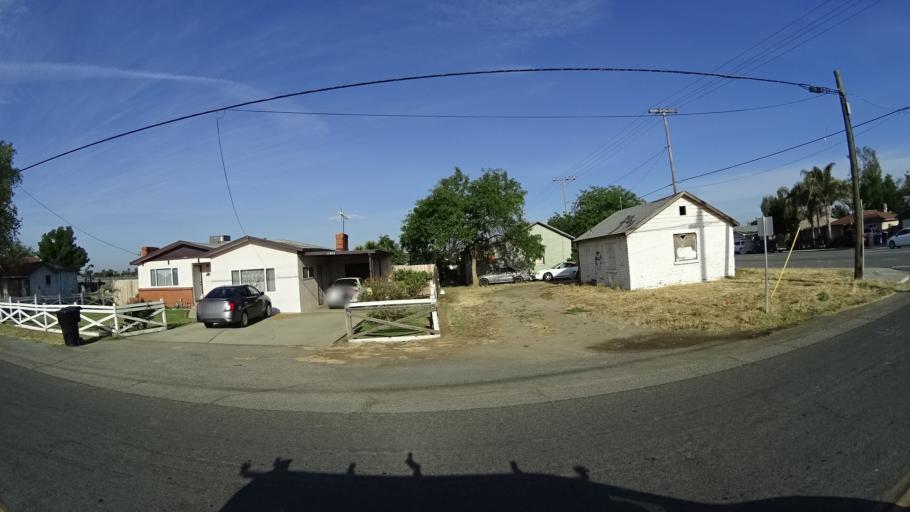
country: US
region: California
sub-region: Kings County
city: Home Garden
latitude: 36.3131
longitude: -119.6460
